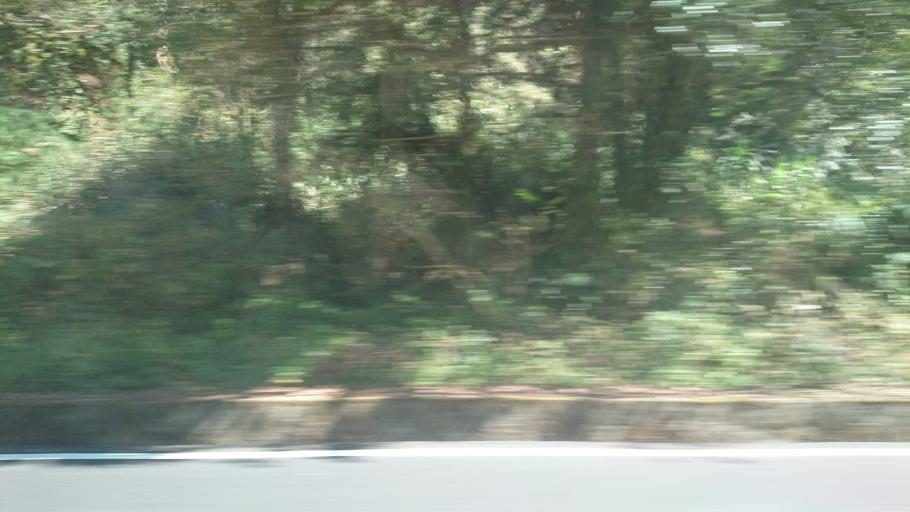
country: TW
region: Taiwan
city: Lugu
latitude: 23.4885
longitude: 120.8210
